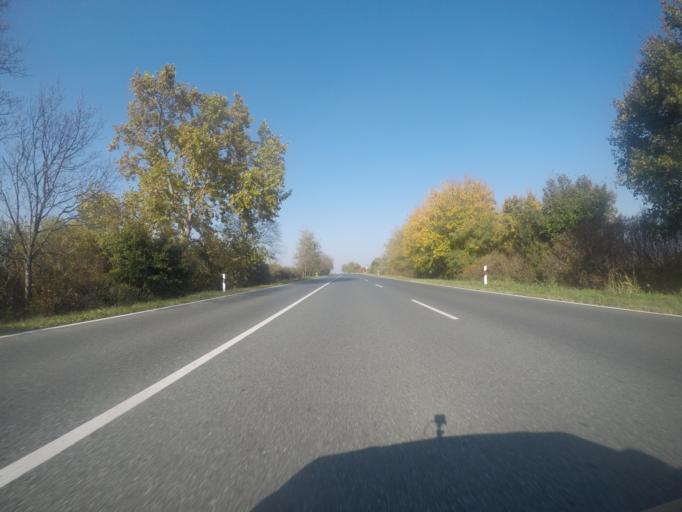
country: HU
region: Tolna
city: Madocsa
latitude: 46.6993
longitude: 18.8876
